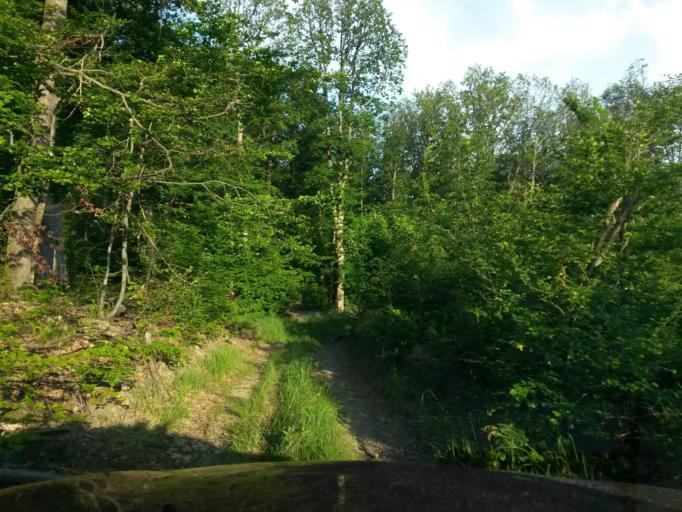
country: SK
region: Kosicky
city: Moldava nad Bodvou
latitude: 48.7340
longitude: 21.0424
